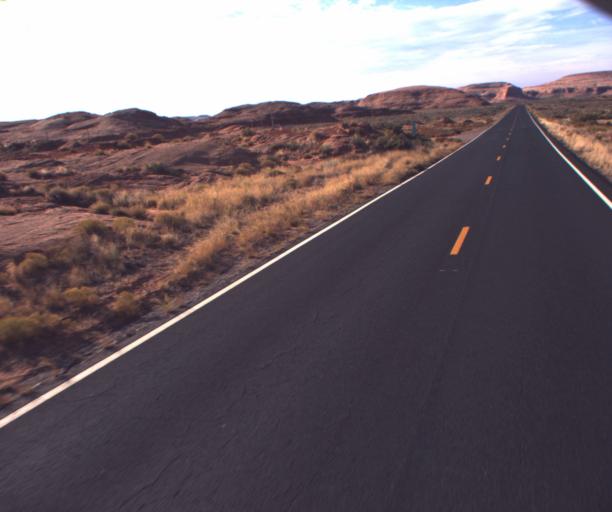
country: US
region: Arizona
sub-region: Apache County
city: Many Farms
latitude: 36.7809
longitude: -109.6577
